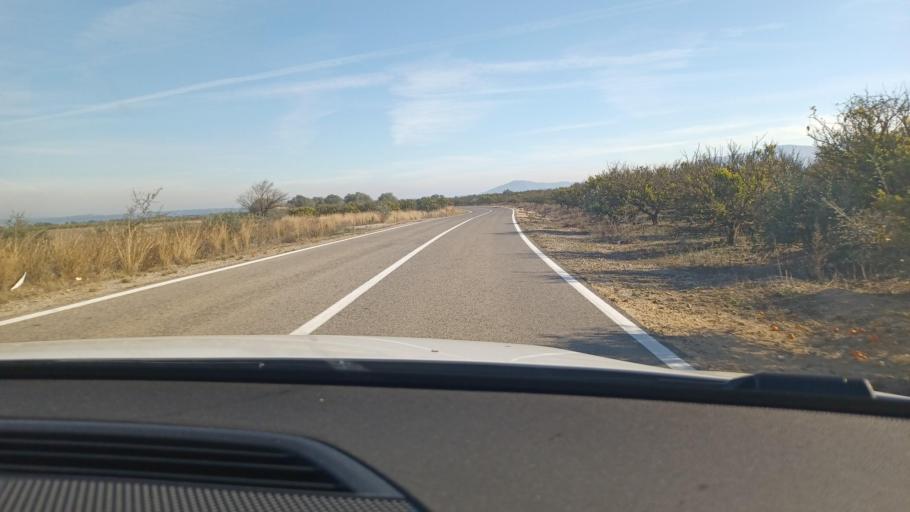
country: ES
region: Catalonia
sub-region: Provincia de Tarragona
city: Santa Barbara
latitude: 40.7220
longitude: 0.4405
